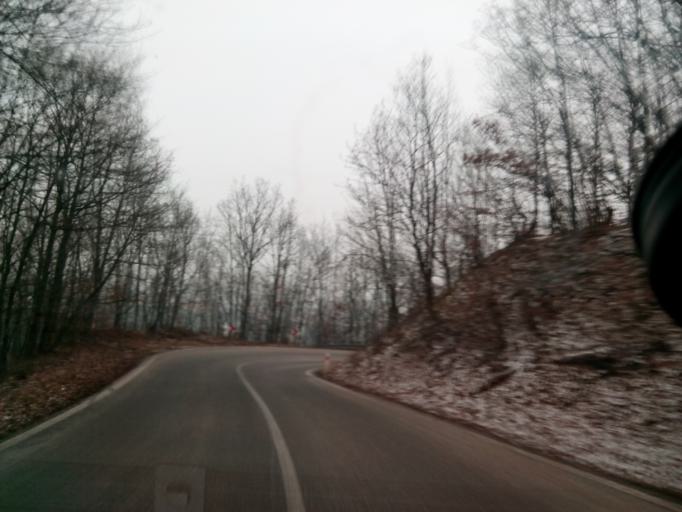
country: SK
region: Kosicky
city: Kosice
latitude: 48.7104
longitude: 21.1978
